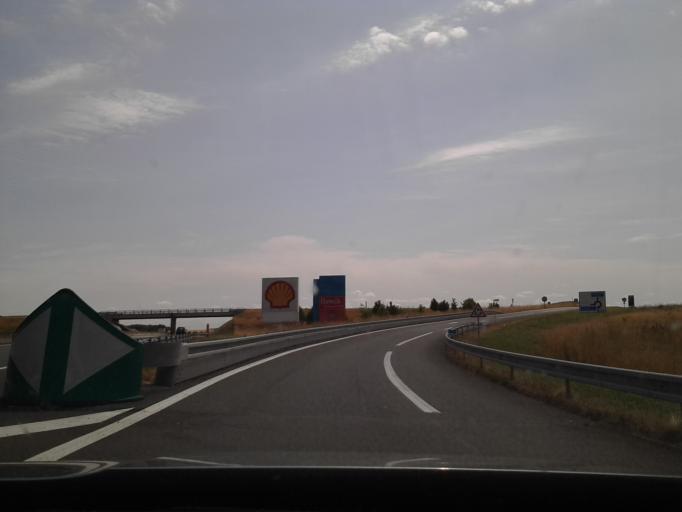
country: FR
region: Centre
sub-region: Departement d'Indre-et-Loire
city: Saint-Christophe-sur-le-Nais
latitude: 47.6497
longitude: 0.4644
